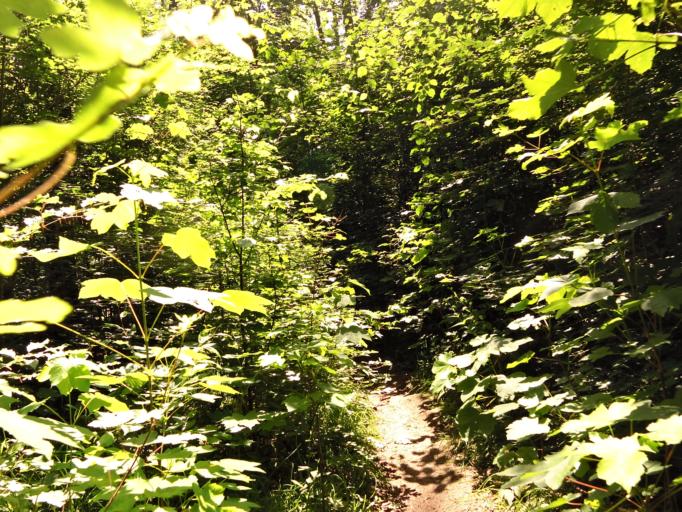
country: DE
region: Bavaria
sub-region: Regierungsbezirk Unterfranken
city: Wuerzburg
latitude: 49.7583
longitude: 9.8809
